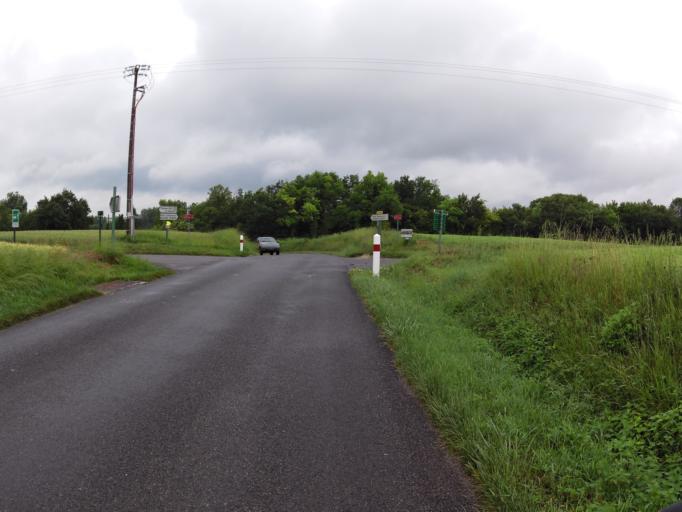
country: FR
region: Poitou-Charentes
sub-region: Departement de la Charente
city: Balzac
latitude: 45.7155
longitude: 0.1290
